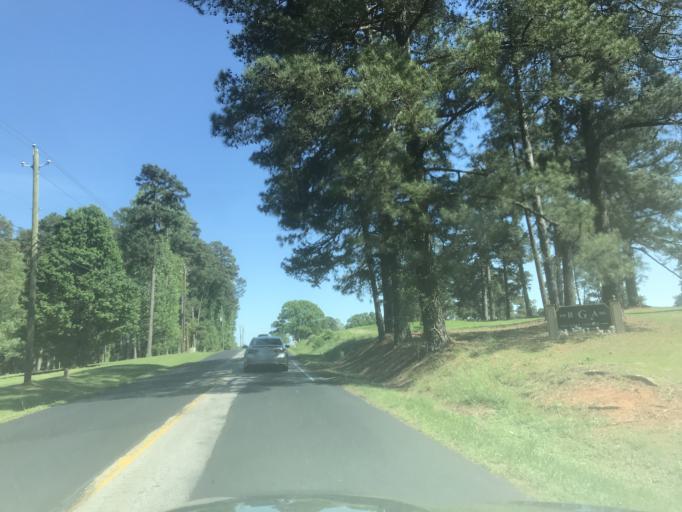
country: US
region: North Carolina
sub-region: Wake County
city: Raleigh
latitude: 35.7389
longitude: -78.6668
